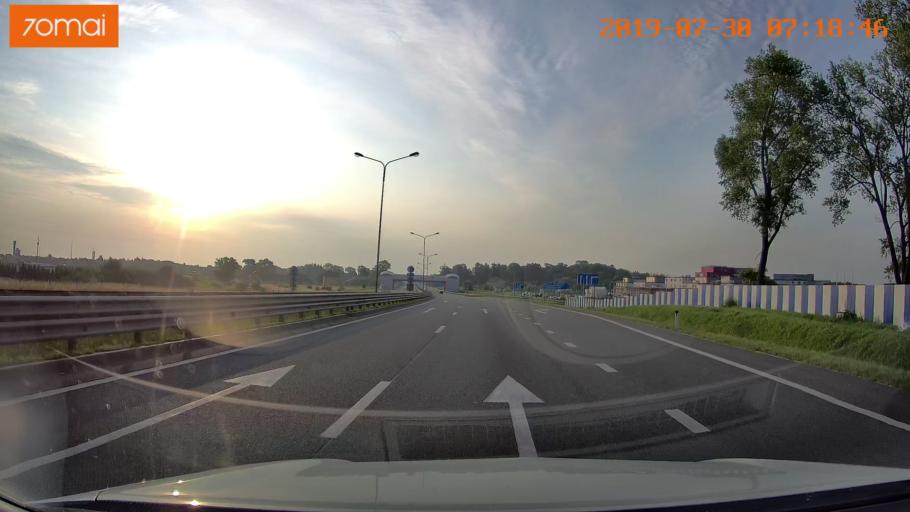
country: RU
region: Kaliningrad
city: Bol'shoe Isakovo
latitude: 54.7026
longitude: 20.6564
